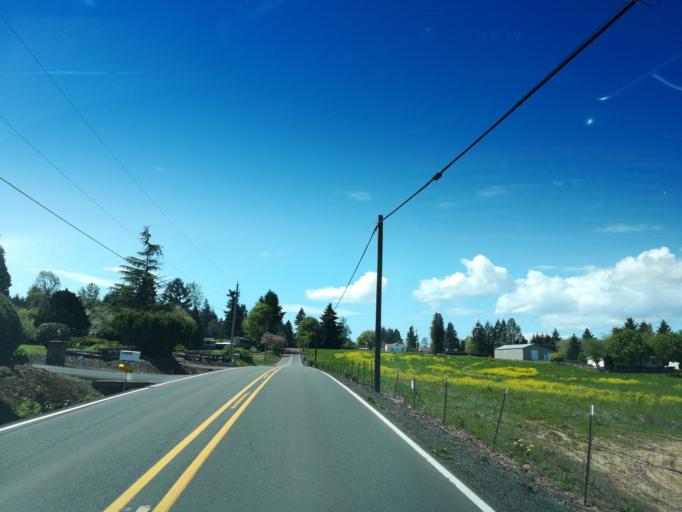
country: US
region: Oregon
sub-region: Clackamas County
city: Damascus
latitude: 45.4325
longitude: -122.4268
